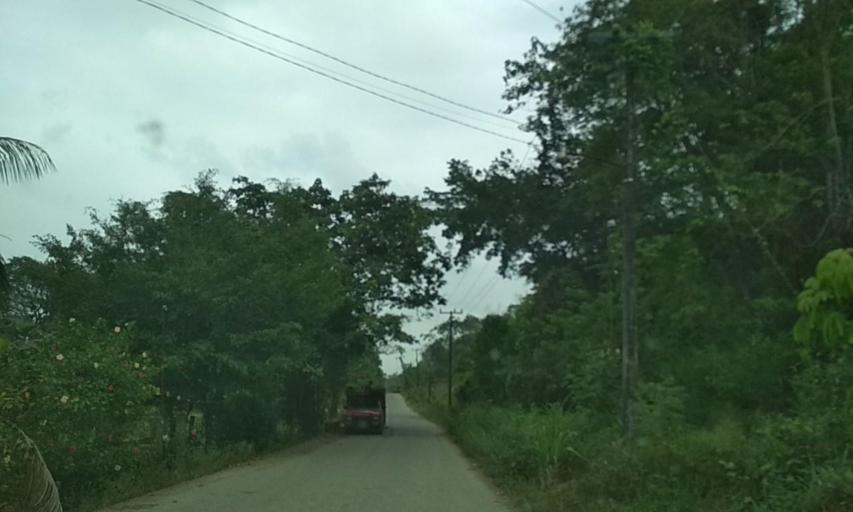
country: MX
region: Veracruz
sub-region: Uxpanapa
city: Poblado 10
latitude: 17.4614
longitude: -94.1055
